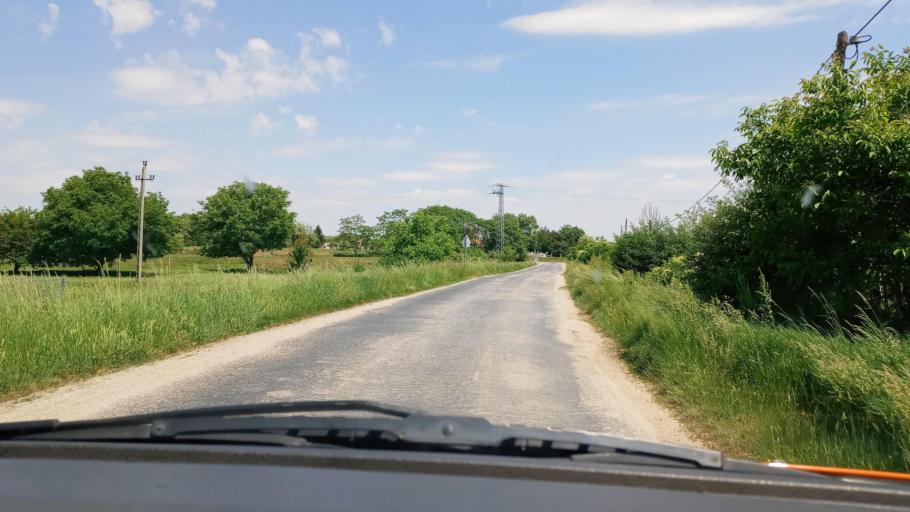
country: HR
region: Osjecko-Baranjska
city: Viljevo
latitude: 45.8253
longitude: 18.0928
